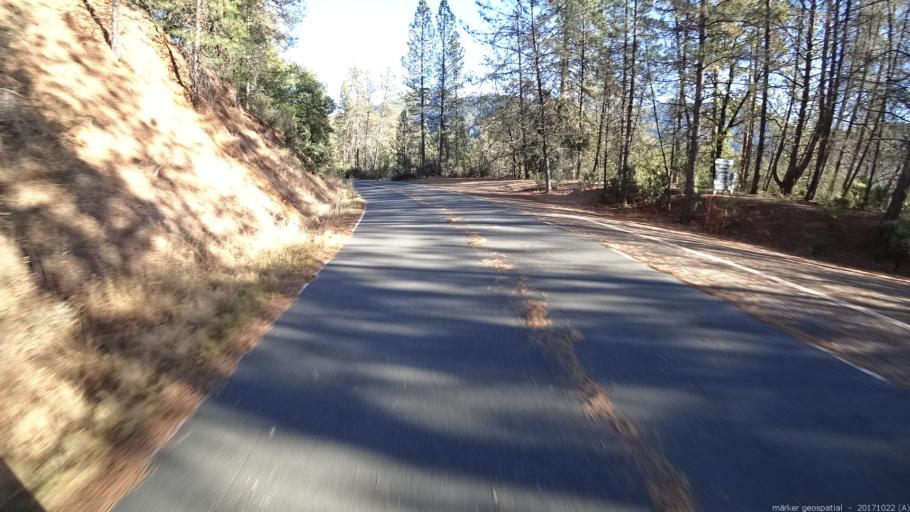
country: US
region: California
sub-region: Shasta County
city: Bella Vista
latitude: 40.8754
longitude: -122.2379
